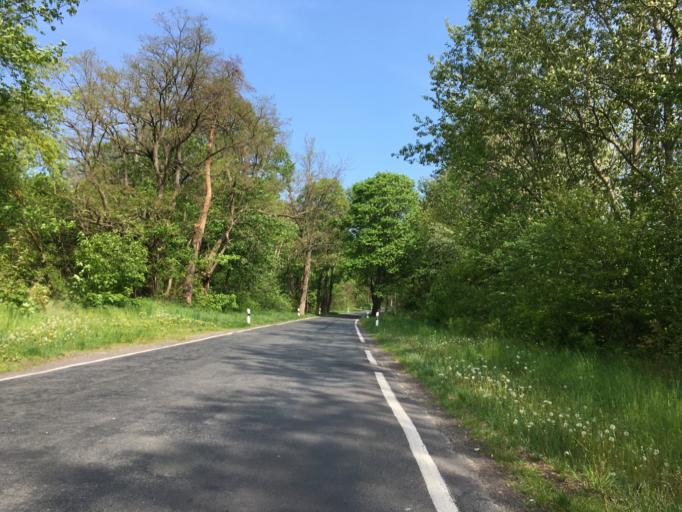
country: DE
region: Brandenburg
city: Werneuchen
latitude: 52.6653
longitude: 13.7318
